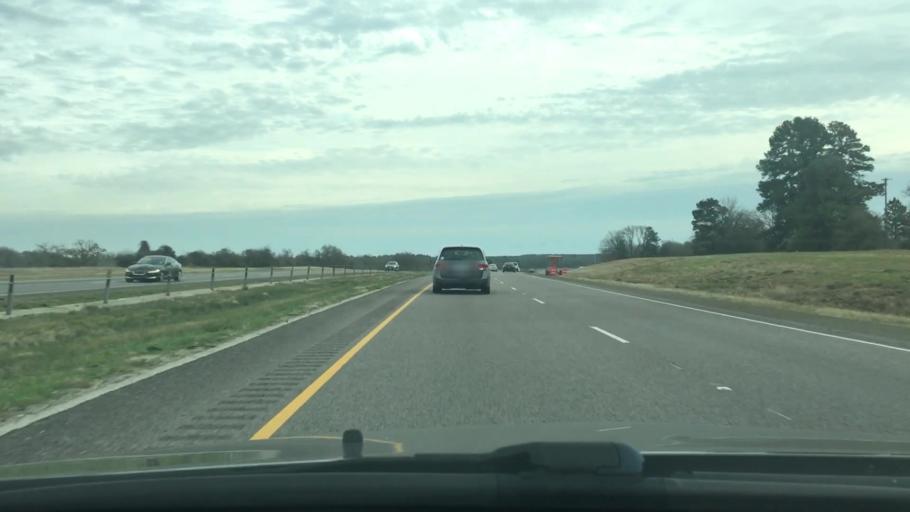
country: US
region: Texas
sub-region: Madison County
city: Madisonville
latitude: 30.9094
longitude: -95.7902
